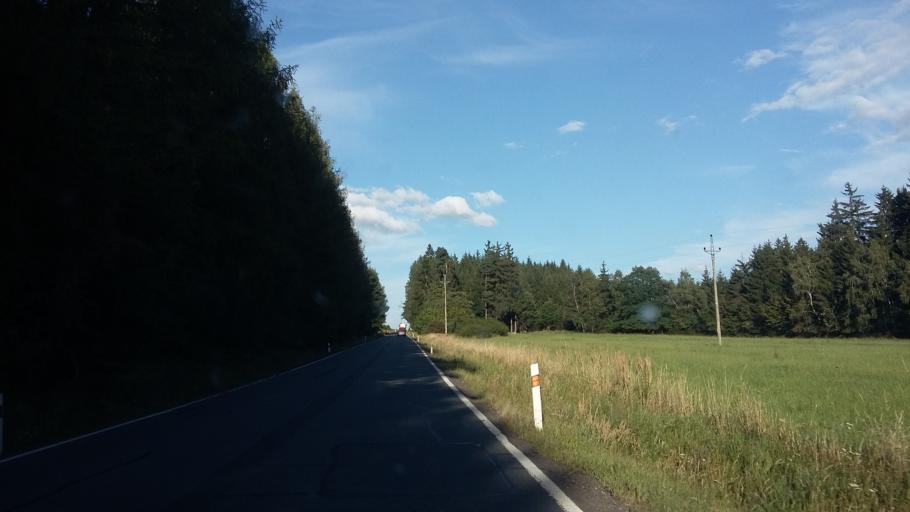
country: CZ
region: Plzensky
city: Mirosov
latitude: 49.6217
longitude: 13.7098
